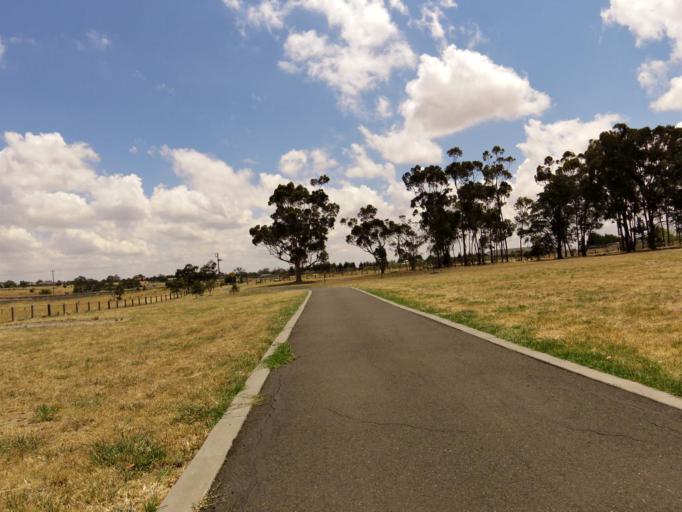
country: AU
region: Victoria
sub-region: Hume
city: Craigieburn
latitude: -37.5677
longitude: 144.9143
